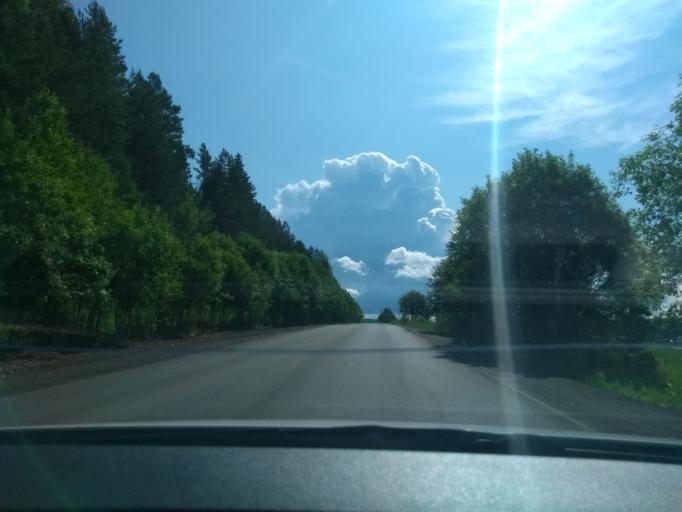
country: RU
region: Perm
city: Kukushtan
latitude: 57.8149
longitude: 56.5466
